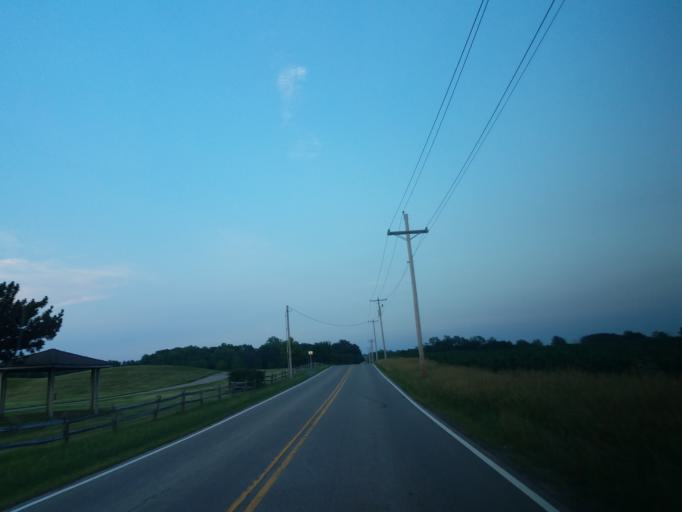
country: US
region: Illinois
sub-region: McLean County
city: Bloomington
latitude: 40.4416
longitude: -89.0049
